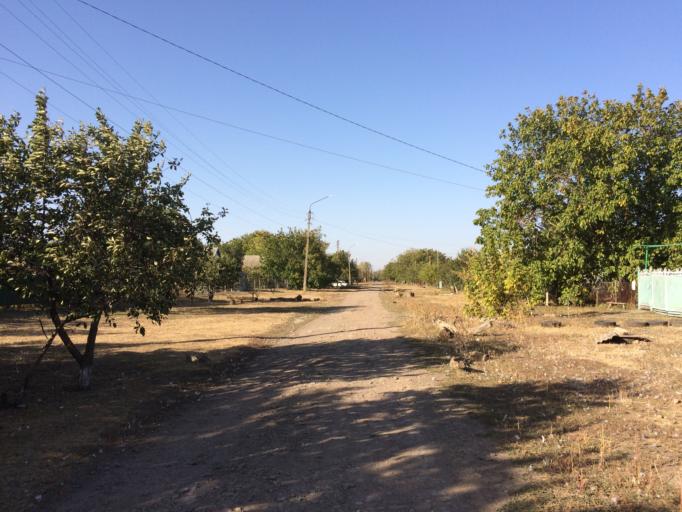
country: RU
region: Rostov
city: Gigant
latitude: 46.5196
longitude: 41.1882
